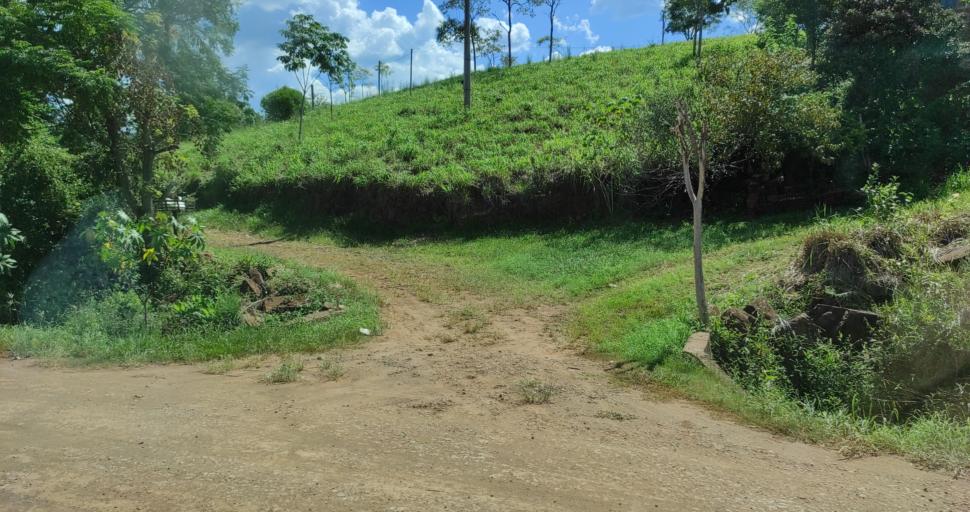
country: AR
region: Misiones
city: El Soberbio
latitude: -27.2788
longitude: -54.1968
